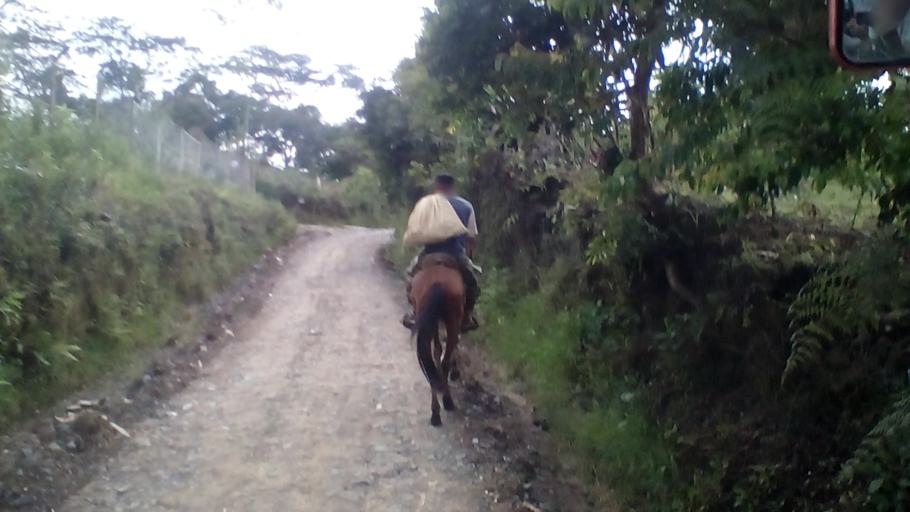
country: CO
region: Boyaca
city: Santana
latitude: 6.0022
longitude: -73.5069
